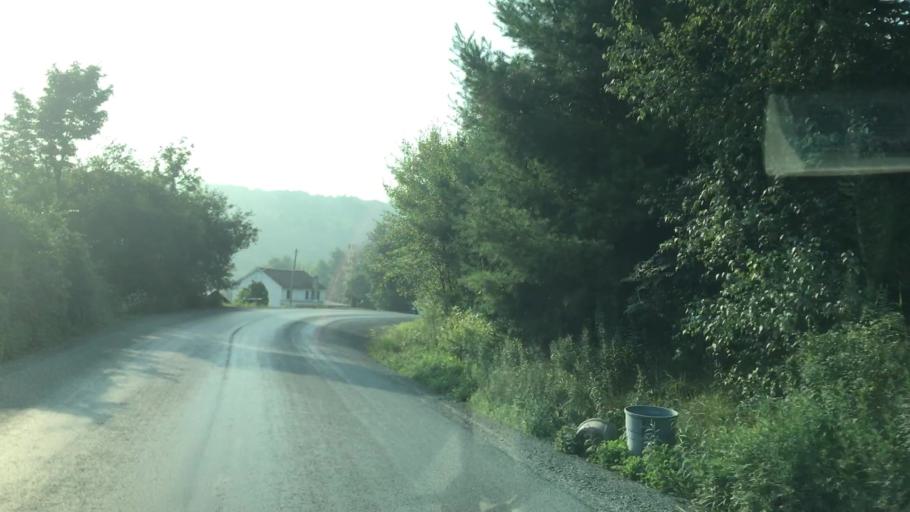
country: US
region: Pennsylvania
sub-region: Wyoming County
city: Factoryville
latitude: 41.6584
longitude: -75.8020
